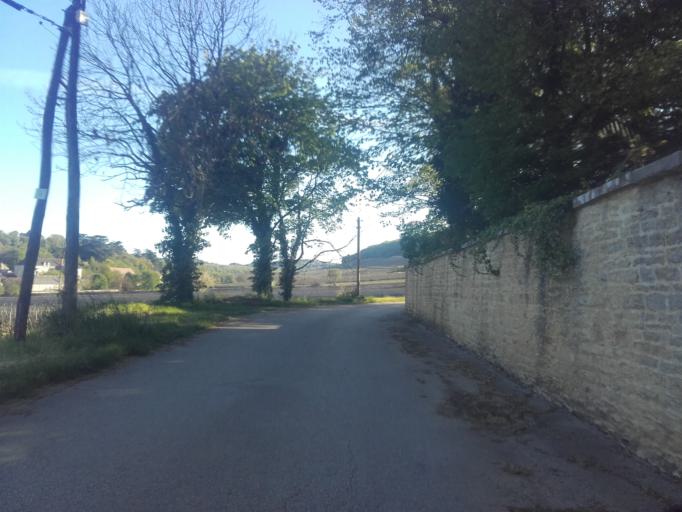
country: FR
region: Bourgogne
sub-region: Departement de Saone-et-Loire
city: Rully
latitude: 46.8772
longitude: 4.7365
